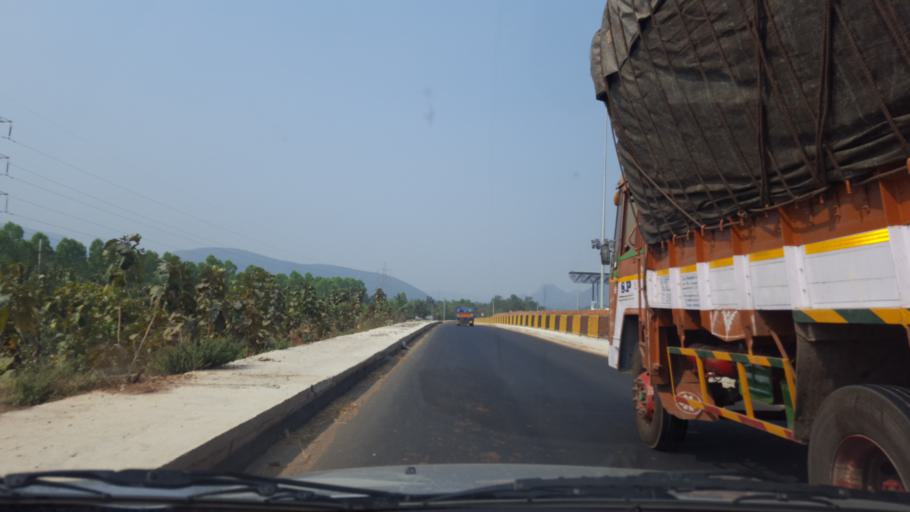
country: IN
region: Andhra Pradesh
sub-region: Vishakhapatnam
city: Bhimunipatnam
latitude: 17.8880
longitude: 83.3470
